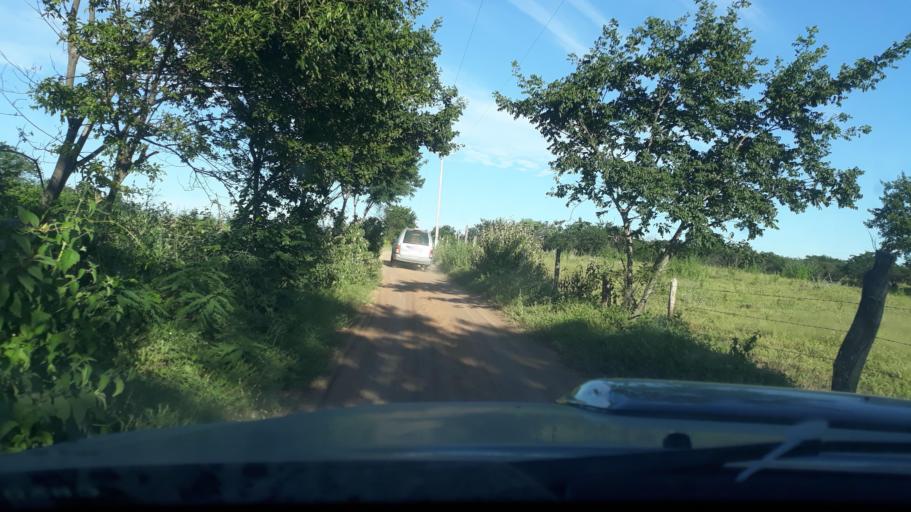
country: BR
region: Bahia
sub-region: Riacho De Santana
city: Riacho de Santana
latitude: -13.8636
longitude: -43.0216
